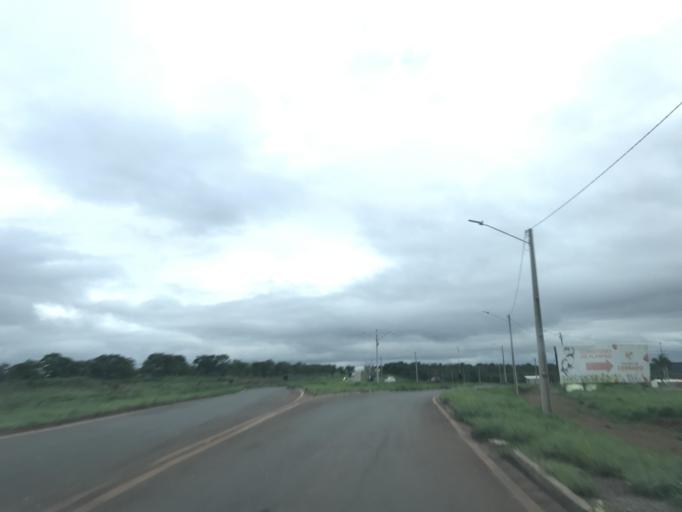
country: BR
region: Goias
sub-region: Luziania
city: Luziania
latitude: -16.2630
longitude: -47.9723
